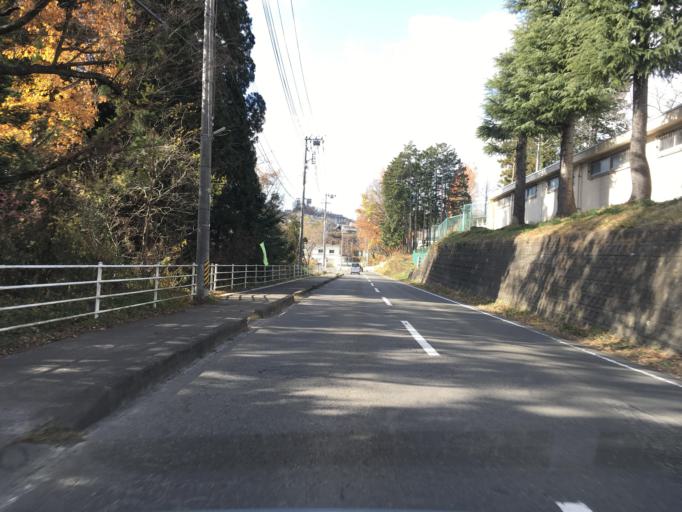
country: JP
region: Miyagi
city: Sendai
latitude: 38.2909
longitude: 140.7506
